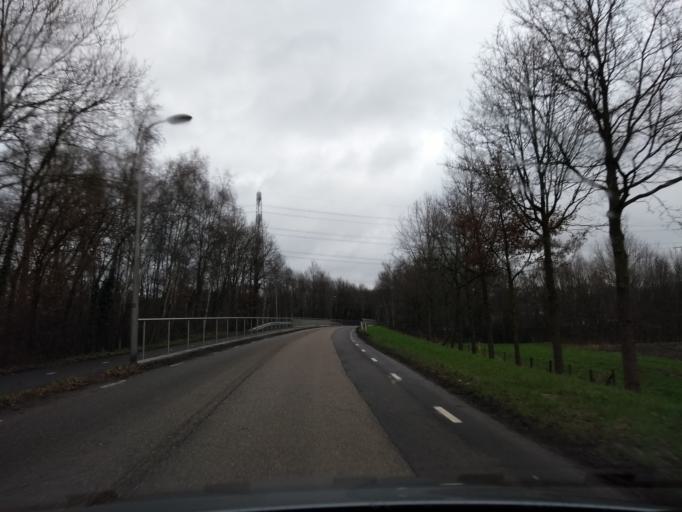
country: NL
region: Overijssel
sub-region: Gemeente Enschede
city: Enschede
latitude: 52.2017
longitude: 6.9236
